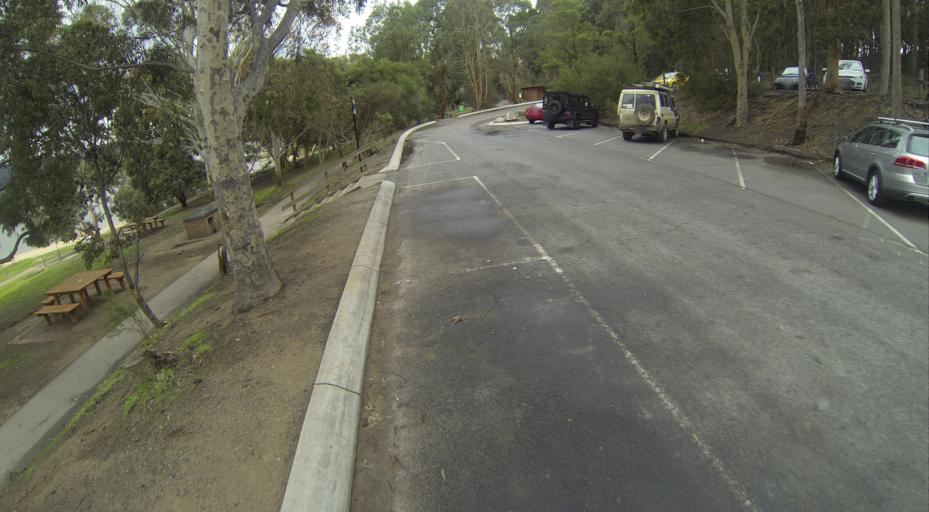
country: AU
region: Victoria
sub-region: Casey
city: Narre Warren North
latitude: -37.9705
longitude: 145.3009
